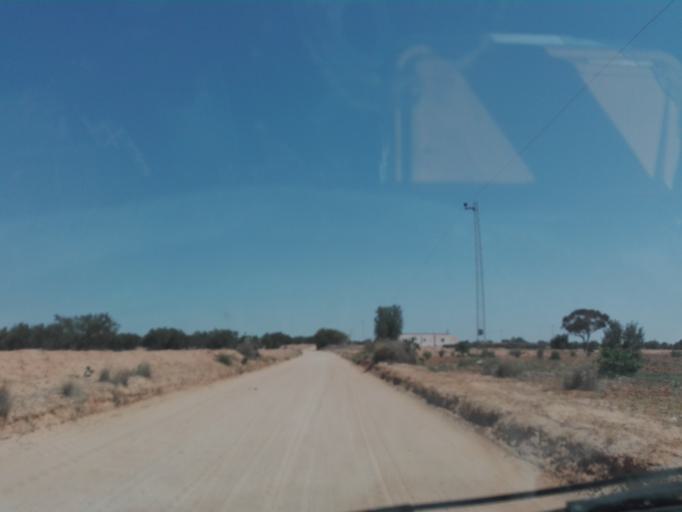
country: TN
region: Safaqis
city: Bi'r `Ali Bin Khalifah
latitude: 34.6609
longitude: 10.2407
